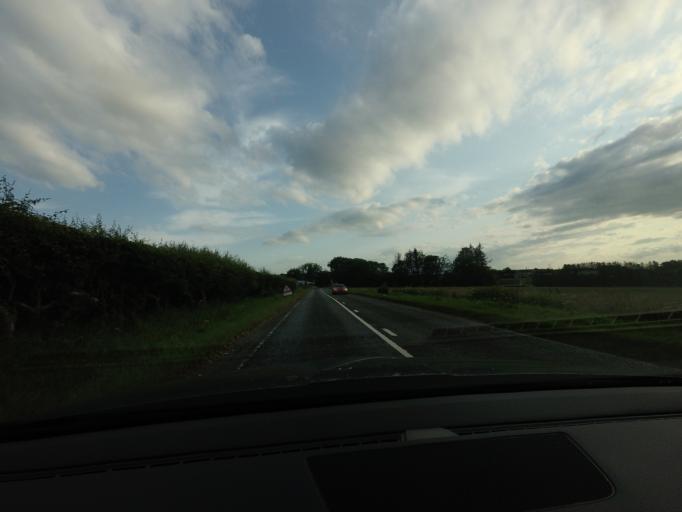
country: GB
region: Scotland
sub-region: Aberdeenshire
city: Turriff
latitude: 57.5463
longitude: -2.4440
